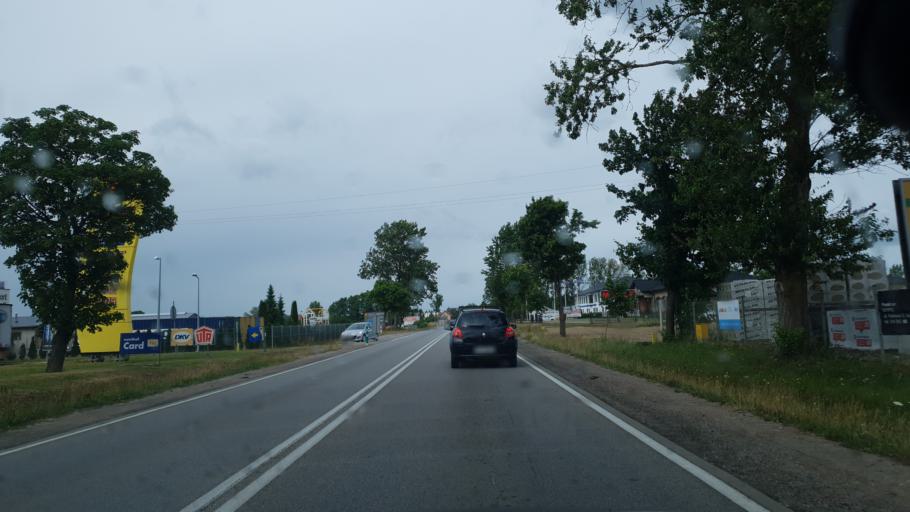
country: PL
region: Pomeranian Voivodeship
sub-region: Powiat kartuski
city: Banino
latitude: 54.4133
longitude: 18.3727
